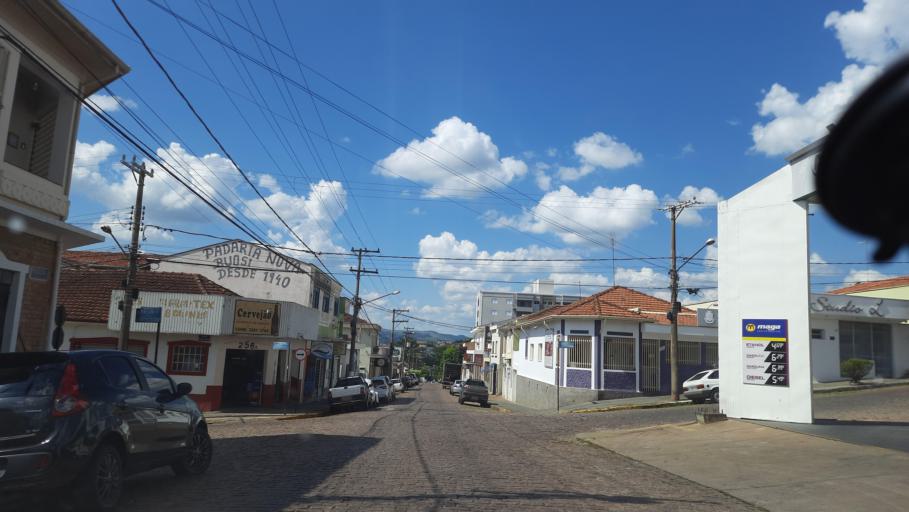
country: BR
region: Sao Paulo
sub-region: Sao Jose Do Rio Pardo
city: Sao Jose do Rio Pardo
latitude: -21.5992
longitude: -46.8946
